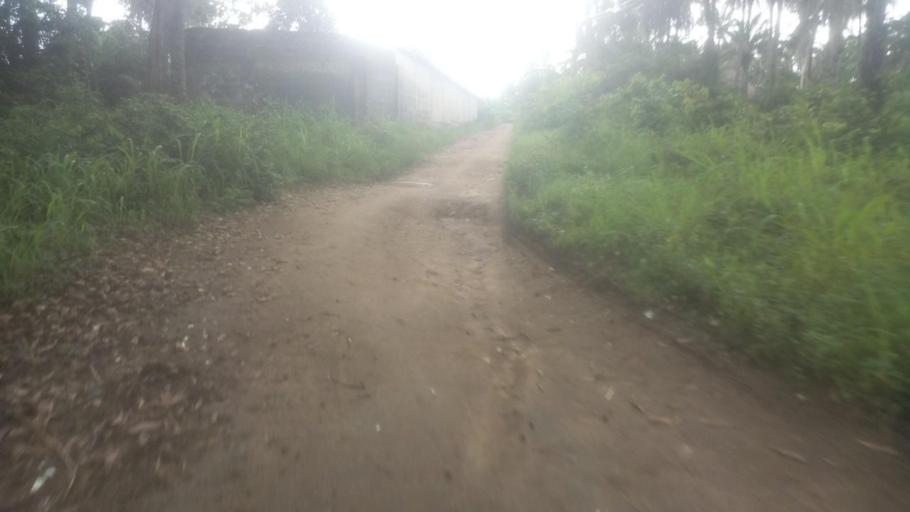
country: SL
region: Northern Province
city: Masoyila
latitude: 8.5779
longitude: -13.1650
